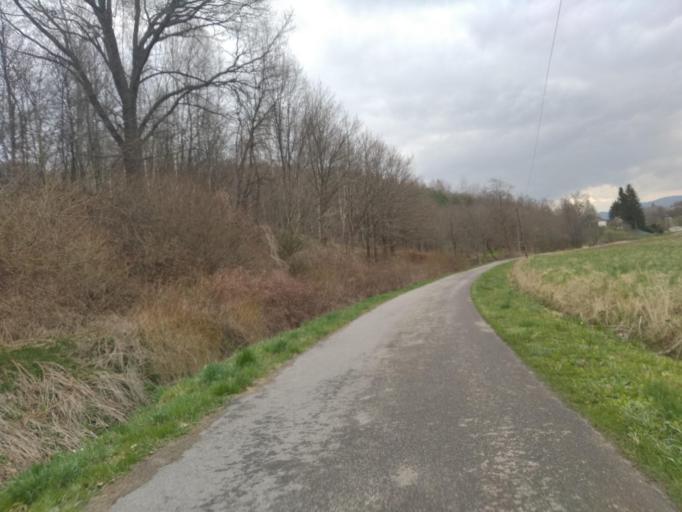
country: PL
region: Subcarpathian Voivodeship
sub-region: Powiat strzyzowski
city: Wisniowa
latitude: 49.8959
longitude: 21.7121
